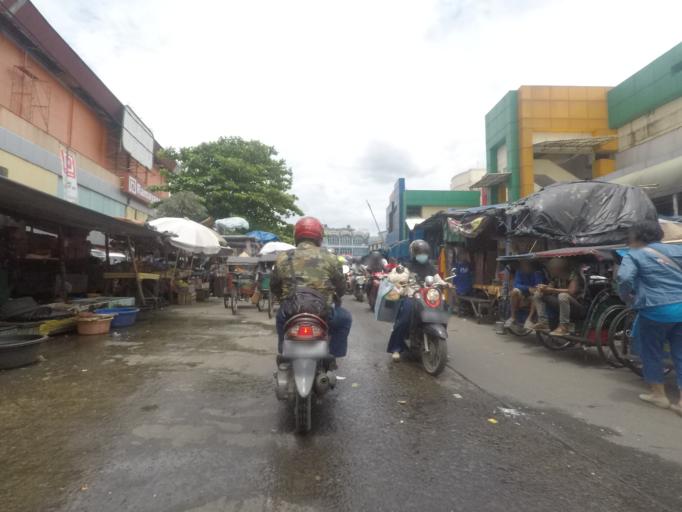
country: ID
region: West Java
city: Bogor
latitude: -6.5907
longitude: 106.7918
